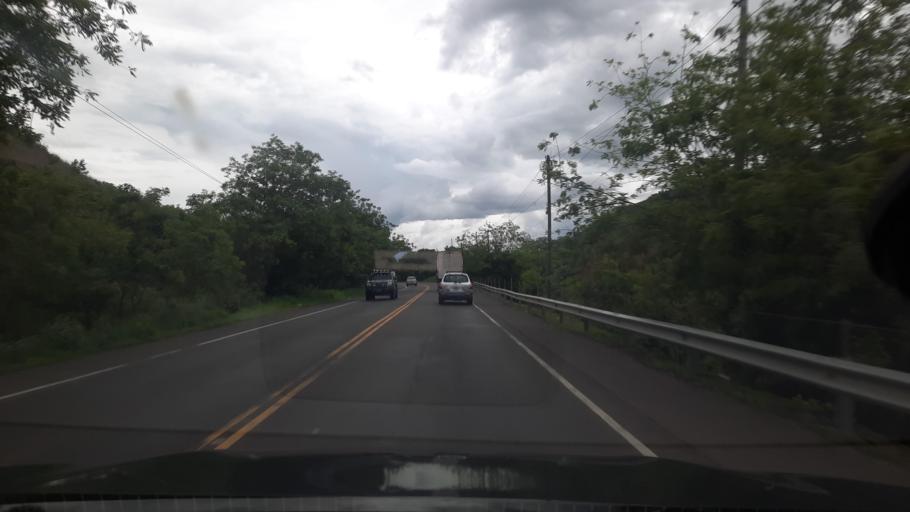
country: HN
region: Choluteca
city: Marcovia
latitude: 13.3582
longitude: -87.2774
